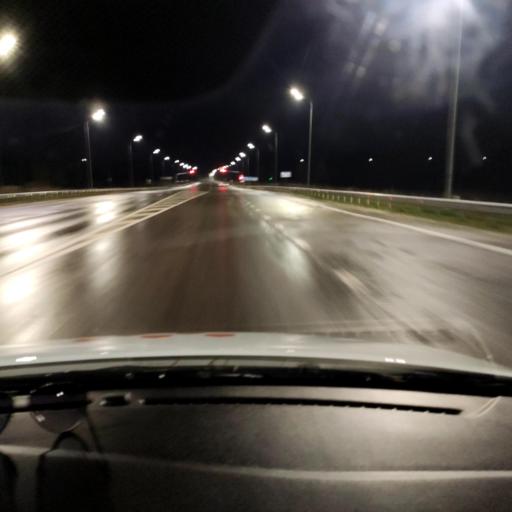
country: RU
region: Tatarstan
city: Stolbishchi
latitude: 55.6389
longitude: 49.1129
